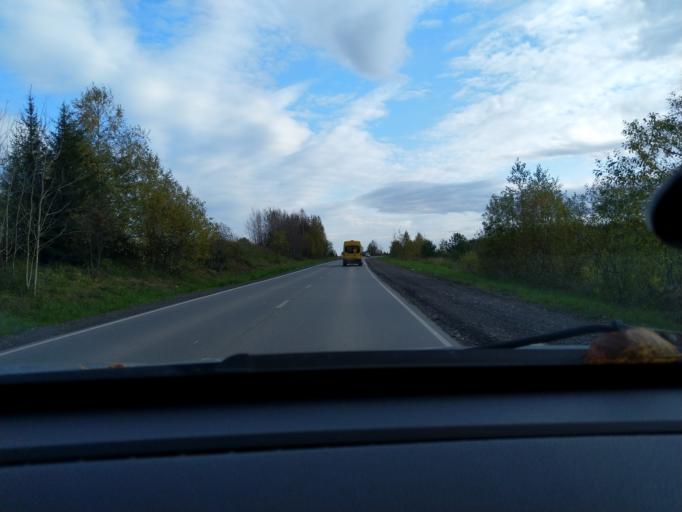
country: RU
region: Perm
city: Polazna
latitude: 58.2779
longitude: 56.4142
